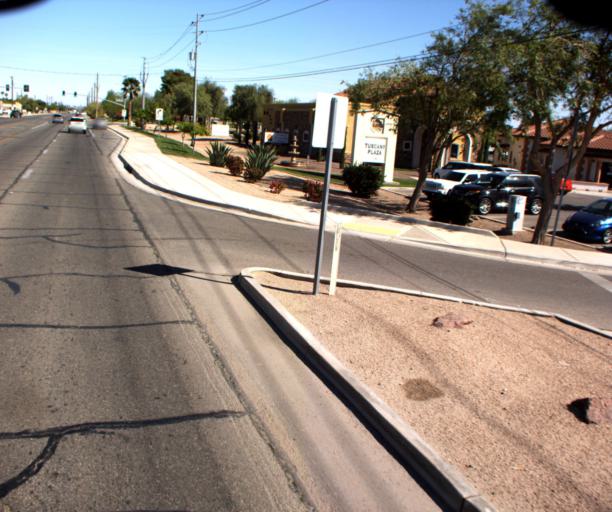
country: US
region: Arizona
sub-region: Yuma County
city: Yuma
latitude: 32.6754
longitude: -114.6502
